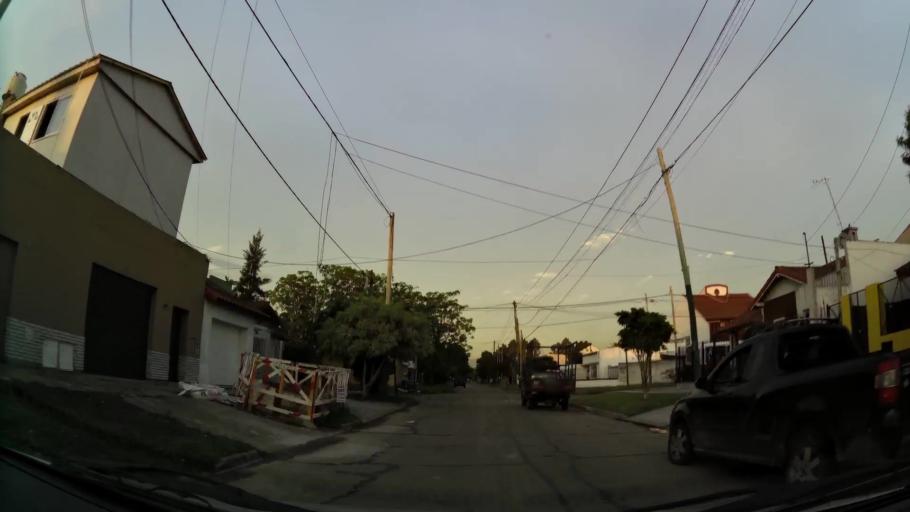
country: AR
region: Buenos Aires
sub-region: Partido de Lomas de Zamora
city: Lomas de Zamora
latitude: -34.7693
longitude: -58.3809
